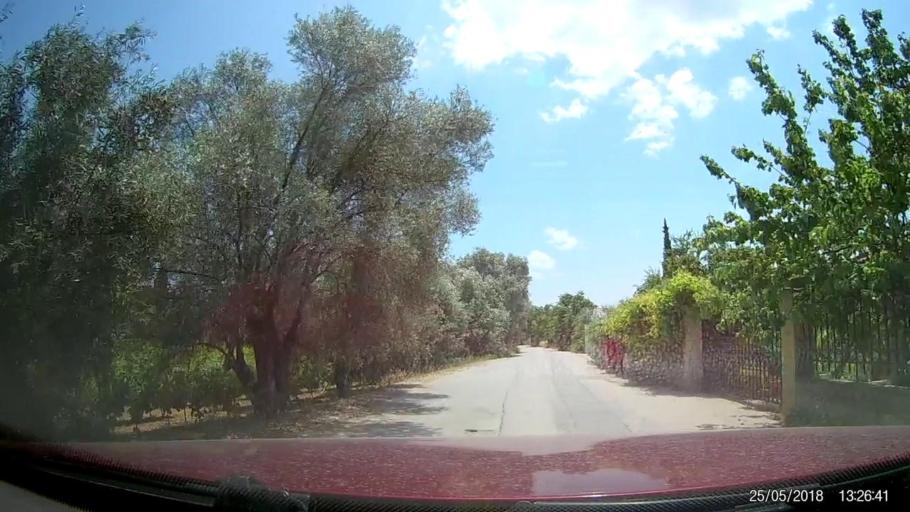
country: GR
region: Central Greece
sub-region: Nomos Evvoias
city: Mytikas
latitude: 38.4547
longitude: 23.6483
